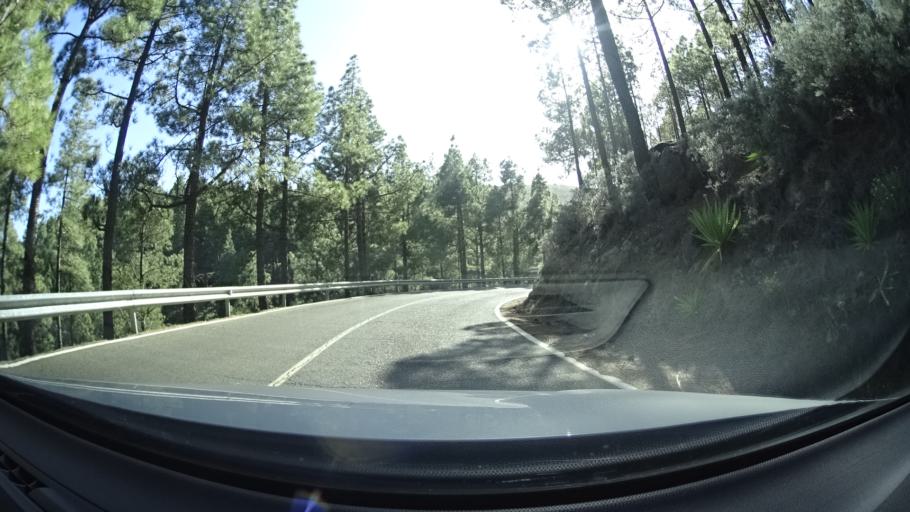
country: ES
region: Canary Islands
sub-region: Provincia de Las Palmas
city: Vega de San Mateo
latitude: 27.9670
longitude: -15.5461
